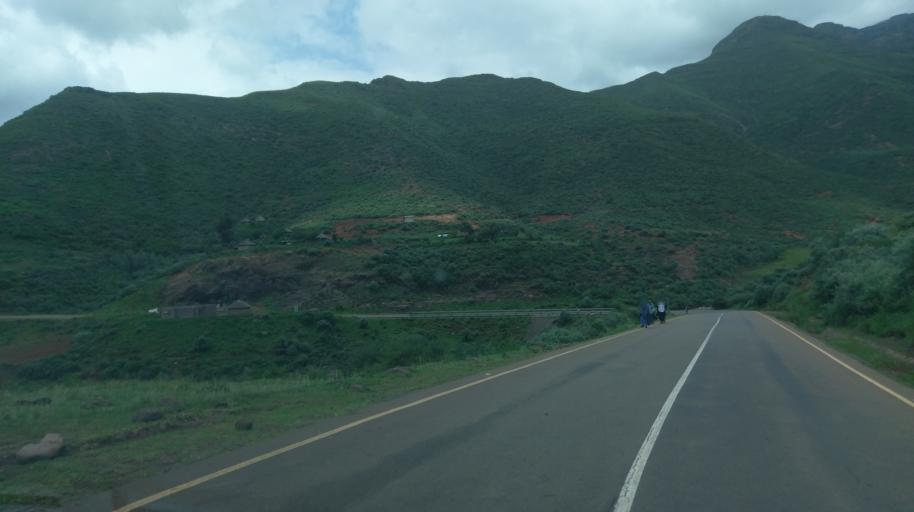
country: LS
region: Butha-Buthe
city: Butha-Buthe
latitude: -29.0463
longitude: 28.3109
